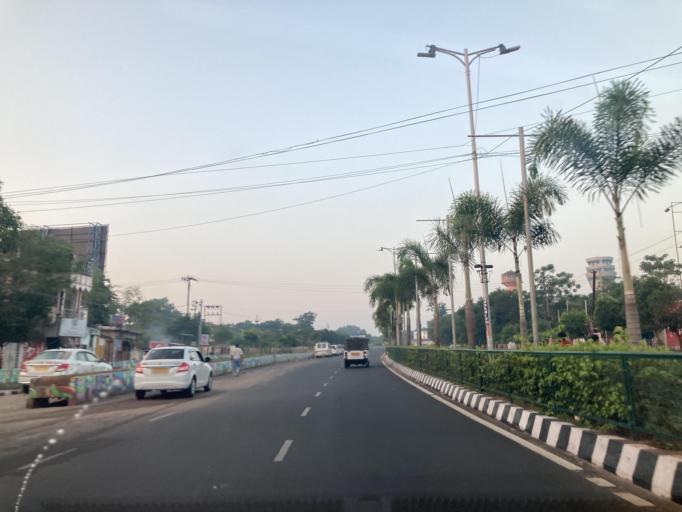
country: IN
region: Odisha
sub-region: Khordha
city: Bhubaneshwar
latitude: 20.2556
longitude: 85.8216
